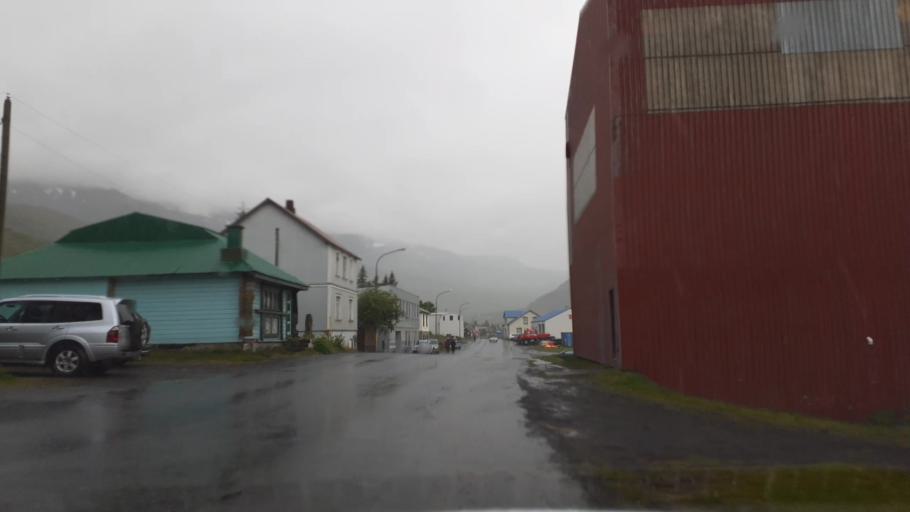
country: IS
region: East
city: Eskifjoerdur
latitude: 65.2652
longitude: -13.9923
